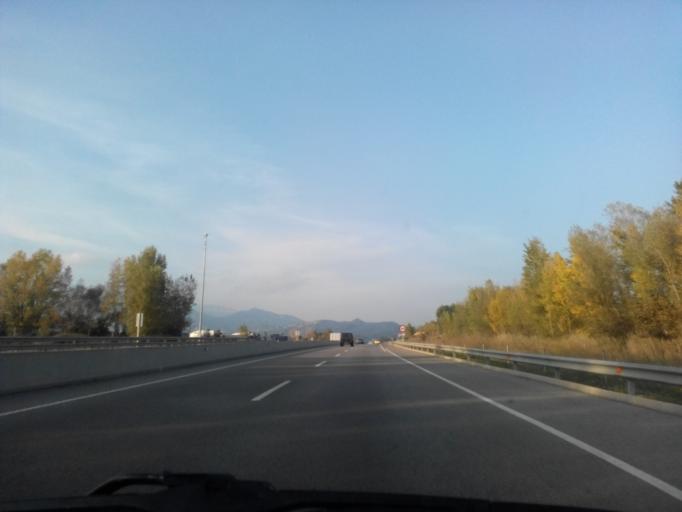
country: ES
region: Catalonia
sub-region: Provincia de Barcelona
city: Gironella
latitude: 42.0505
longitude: 1.8760
